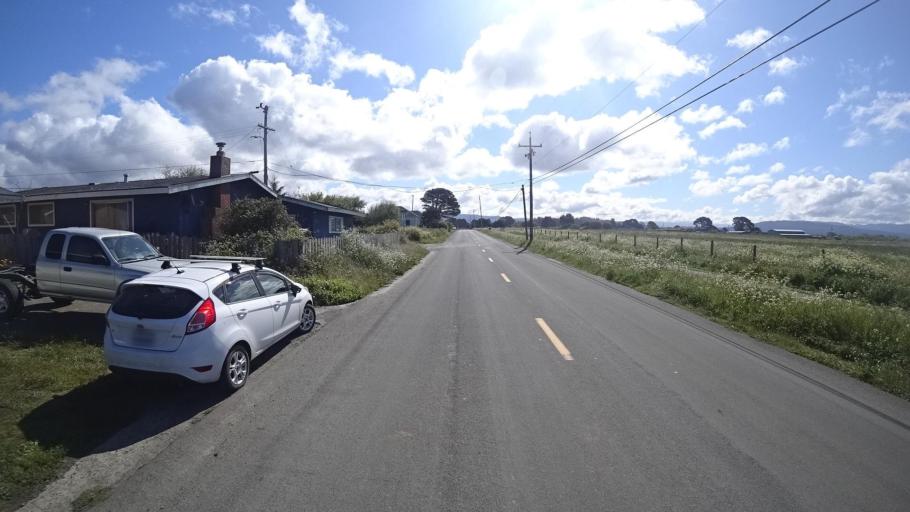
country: US
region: California
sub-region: Humboldt County
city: McKinleyville
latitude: 40.9339
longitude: -124.1248
